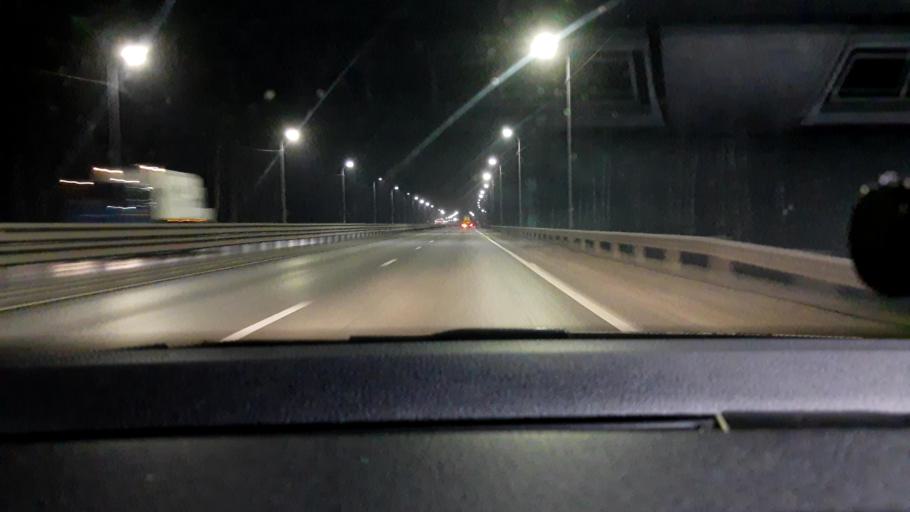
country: RU
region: Moskovskaya
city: Malaya Dubna
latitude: 55.8717
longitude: 38.9429
